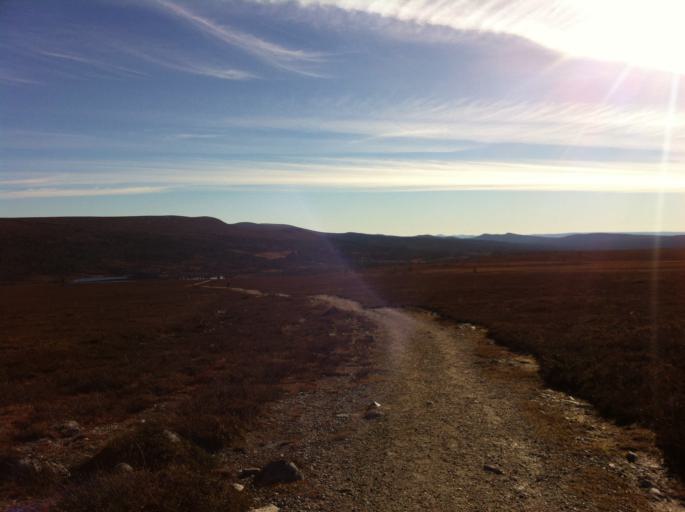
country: NO
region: Hedmark
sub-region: Engerdal
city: Engerdal
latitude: 62.1160
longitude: 12.2629
